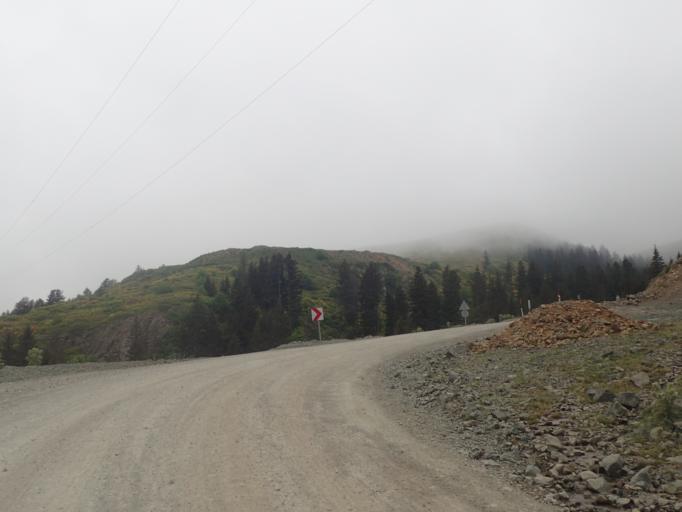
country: TR
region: Ordu
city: Topcam
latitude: 40.6507
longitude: 37.9420
